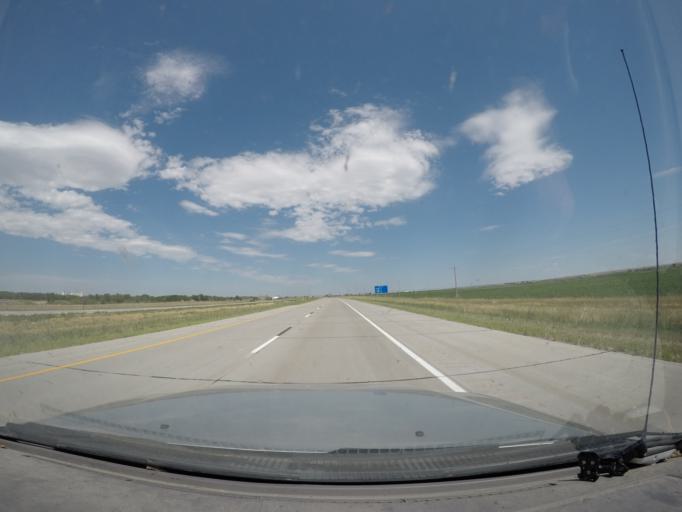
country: US
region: Colorado
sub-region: Sedgwick County
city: Julesburg
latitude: 41.0435
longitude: -102.0882
